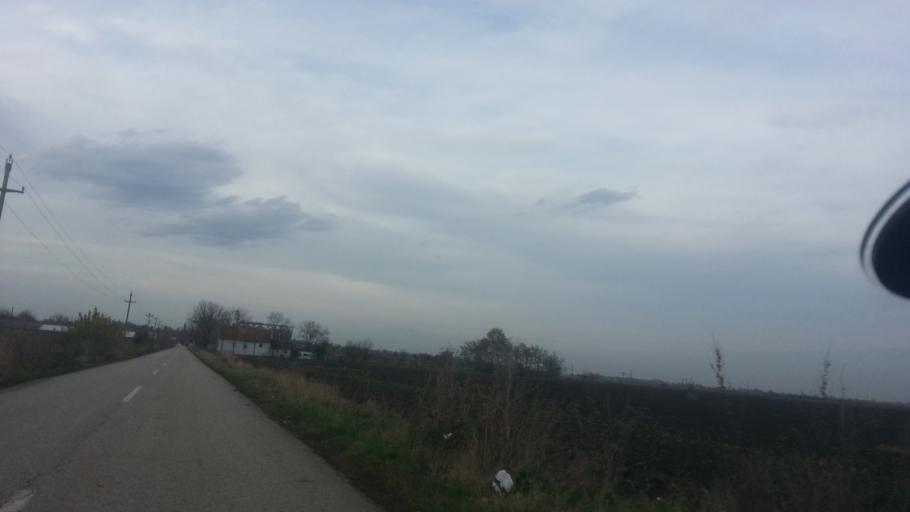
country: RS
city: Putinci
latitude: 44.9769
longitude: 19.9704
